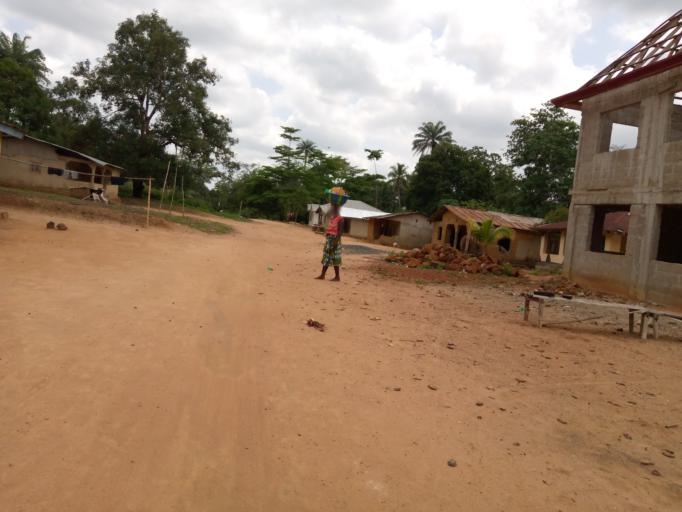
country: SL
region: Western Area
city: Waterloo
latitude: 8.4046
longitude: -12.9496
